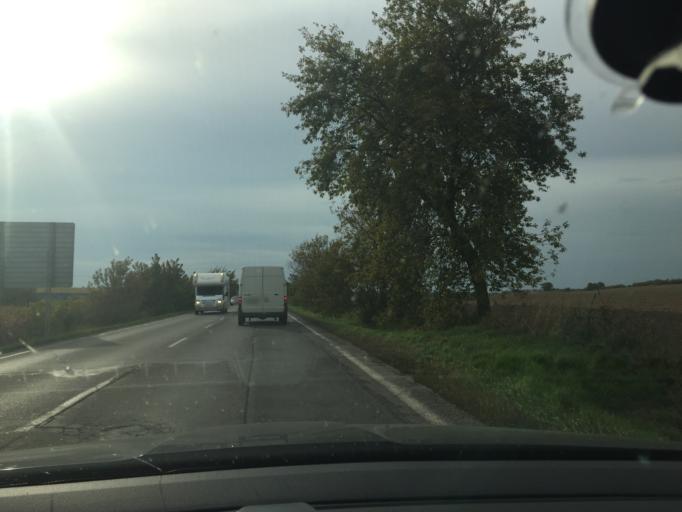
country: CZ
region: Central Bohemia
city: Zelenec
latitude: 50.1221
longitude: 14.6699
